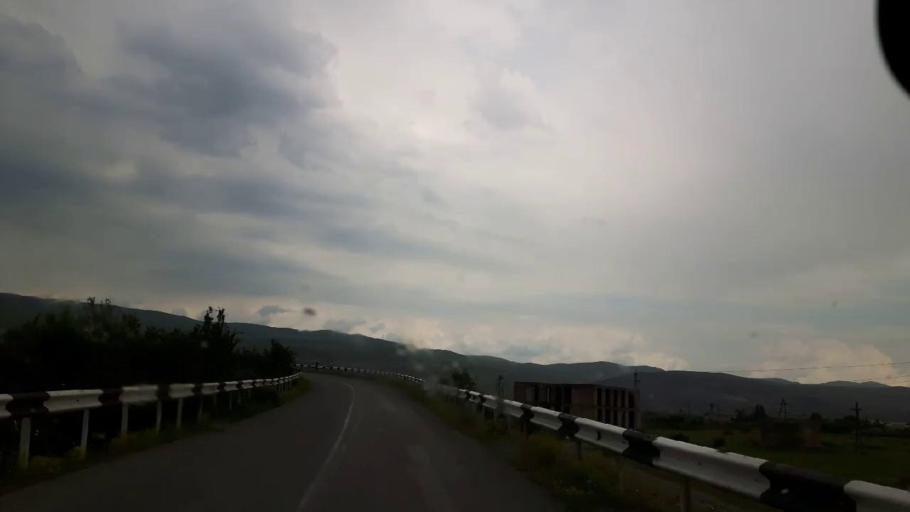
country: GE
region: Shida Kartli
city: Gori
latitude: 41.9638
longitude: 44.1852
